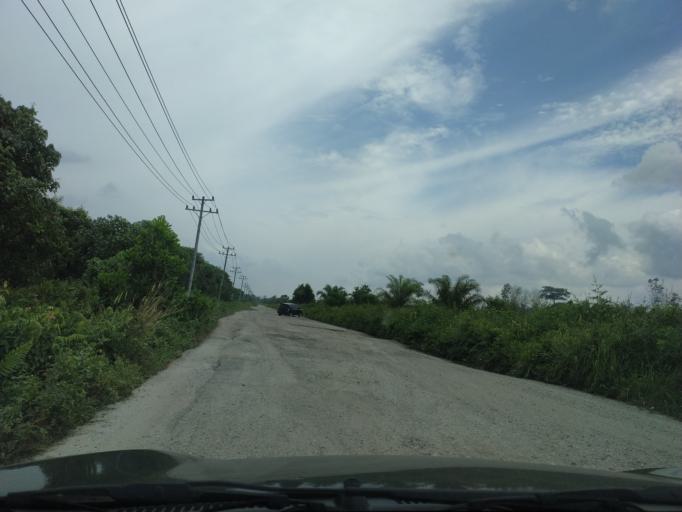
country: ID
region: Riau
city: Siak Sri Indrapura
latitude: 0.9129
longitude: 102.3027
